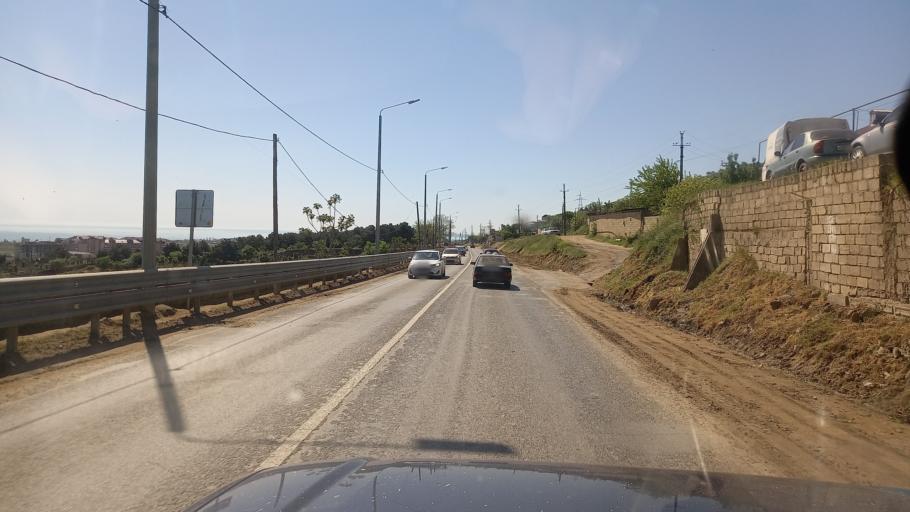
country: RU
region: Dagestan
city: Derbent
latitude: 42.0491
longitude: 48.2824
